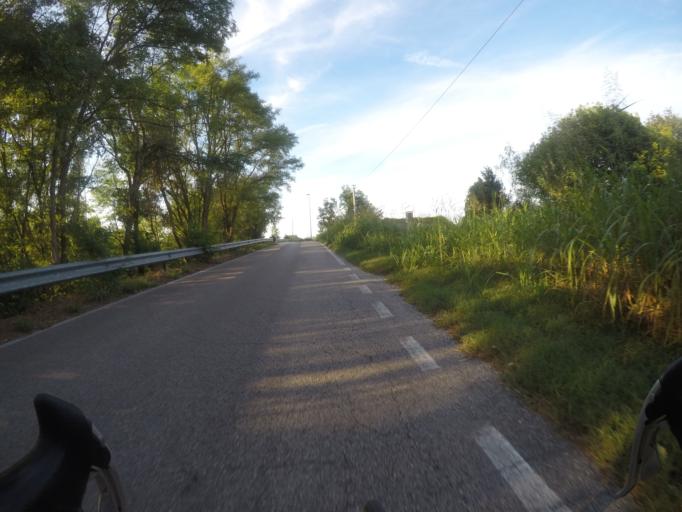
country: IT
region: Veneto
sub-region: Provincia di Rovigo
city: Castelguglielmo
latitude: 45.0132
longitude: 11.5656
